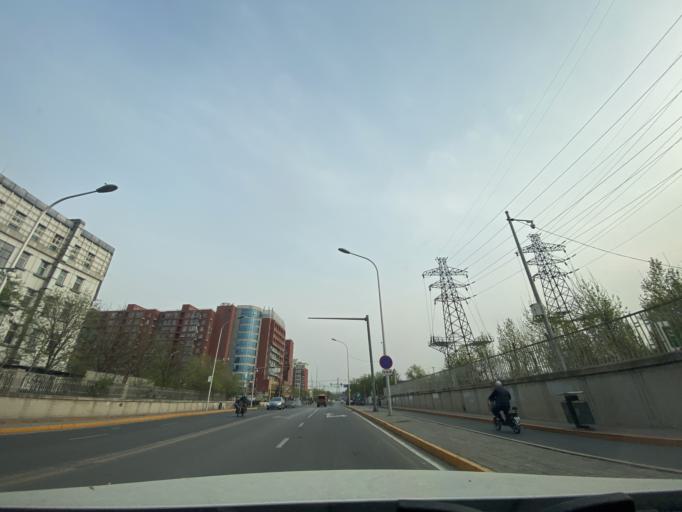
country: CN
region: Beijing
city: Babaoshan
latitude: 39.9291
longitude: 116.2328
